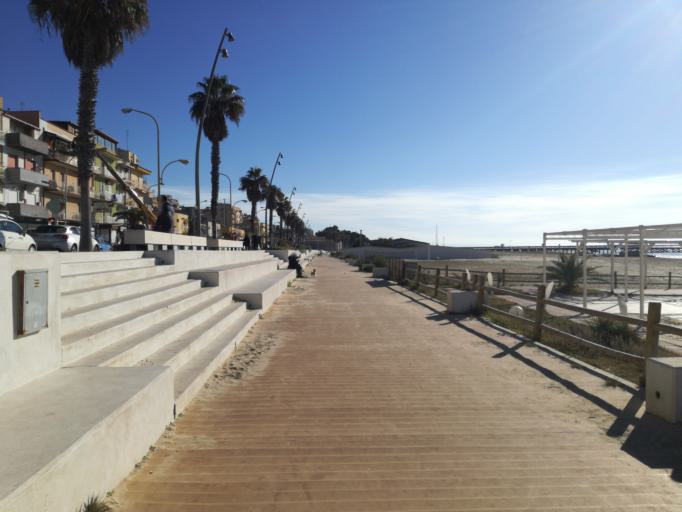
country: IT
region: Sicily
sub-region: Provincia di Caltanissetta
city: Gela
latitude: 37.0656
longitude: 14.2437
